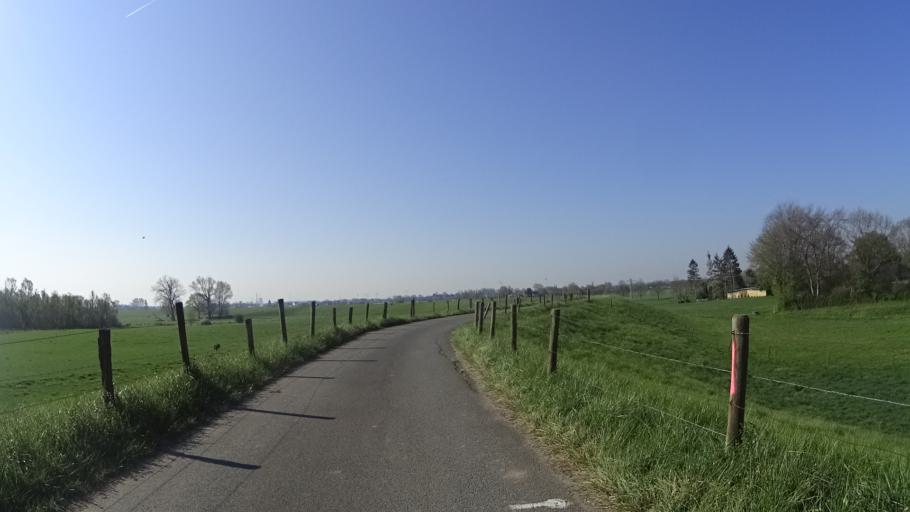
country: DE
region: North Rhine-Westphalia
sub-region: Regierungsbezirk Dusseldorf
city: Alpen
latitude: 51.6096
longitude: 6.5737
